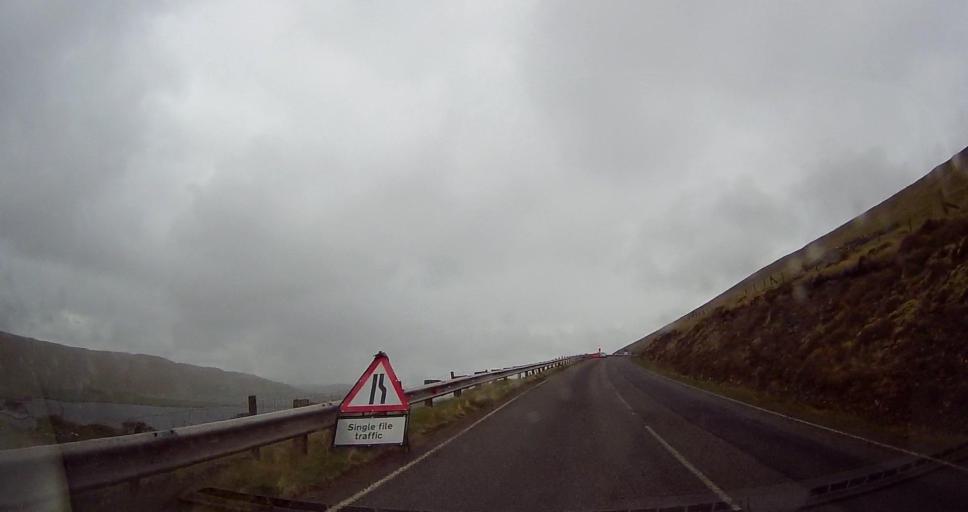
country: GB
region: Scotland
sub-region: Shetland Islands
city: Lerwick
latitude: 60.2479
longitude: -1.3020
